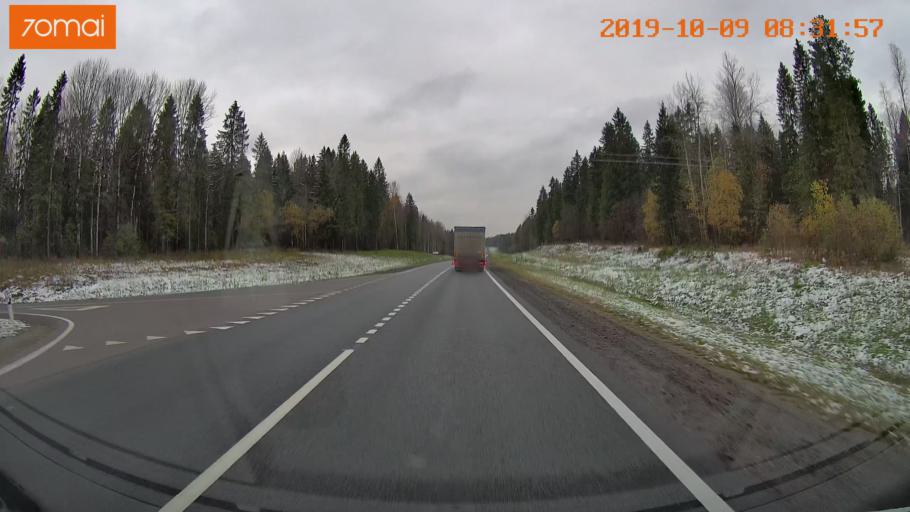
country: RU
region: Vologda
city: Gryazovets
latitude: 58.8603
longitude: 40.1990
